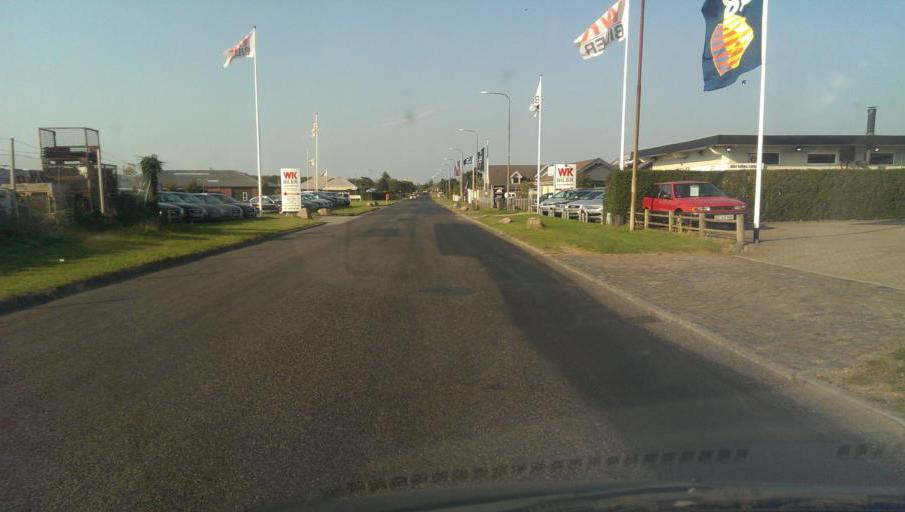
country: DK
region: South Denmark
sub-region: Esbjerg Kommune
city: Esbjerg
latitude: 55.5054
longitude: 8.4175
